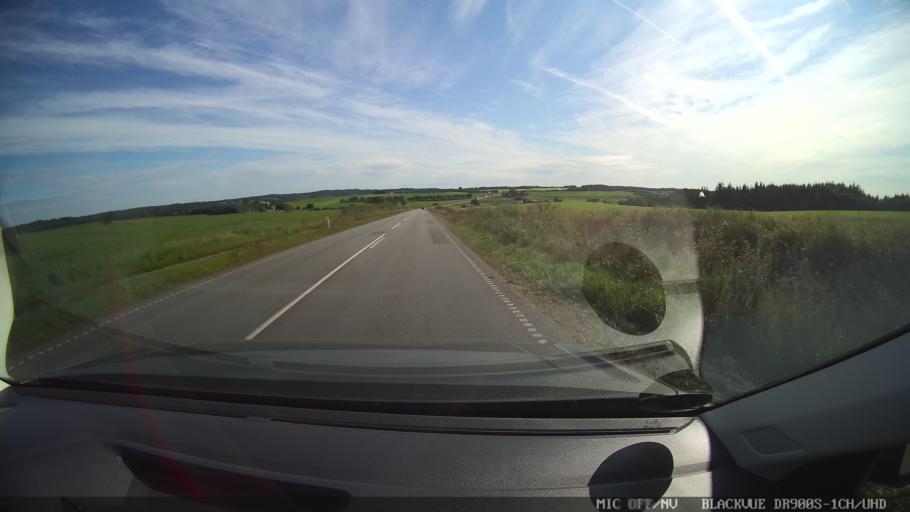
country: DK
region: North Denmark
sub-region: Mariagerfjord Kommune
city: Arden
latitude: 56.7646
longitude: 9.8857
